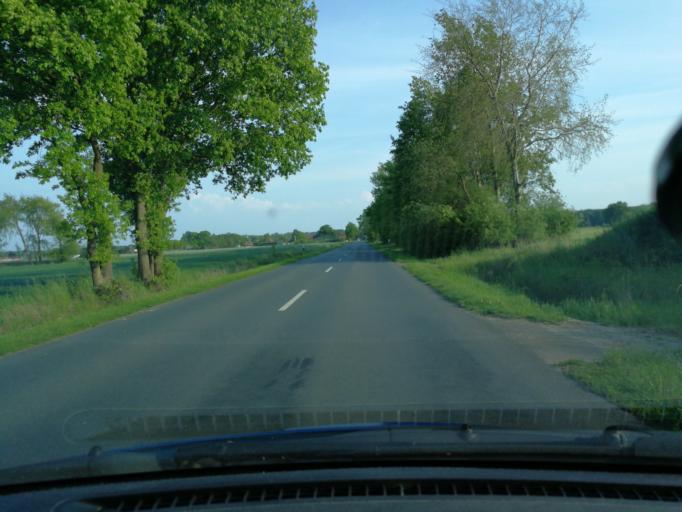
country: DE
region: Lower Saxony
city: Scharnebeck
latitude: 53.3037
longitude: 10.5041
